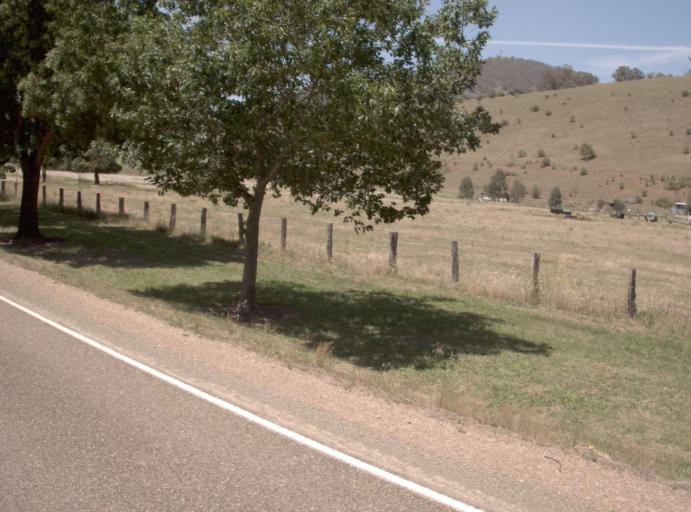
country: AU
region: Victoria
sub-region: East Gippsland
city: Bairnsdale
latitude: -37.2580
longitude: 147.7127
